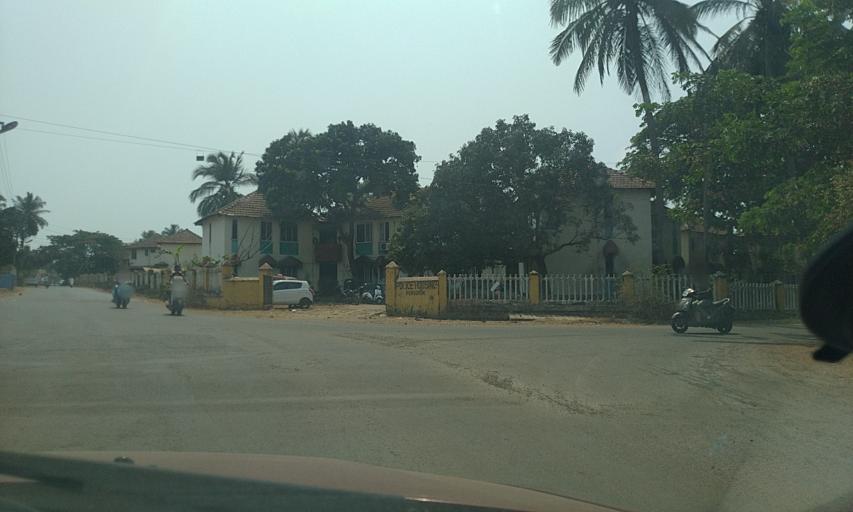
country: IN
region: Goa
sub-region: North Goa
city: Serula
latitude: 15.5255
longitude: 73.8350
